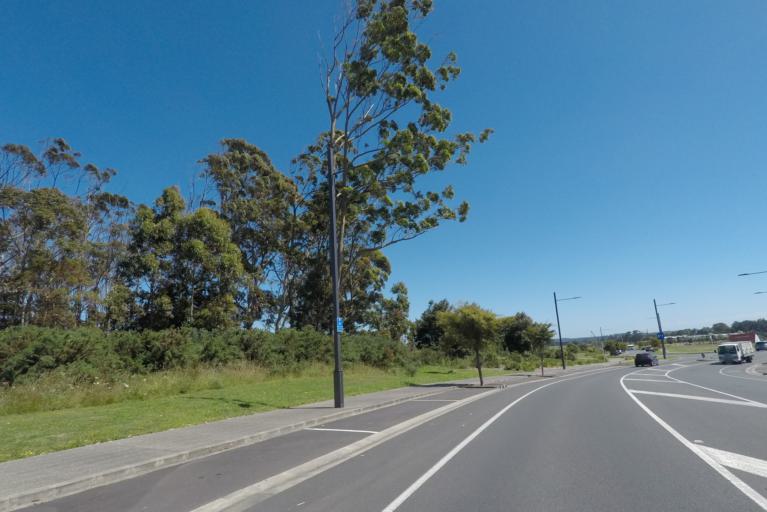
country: NZ
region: Auckland
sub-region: Auckland
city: Rosebank
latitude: -36.8182
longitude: 174.6080
